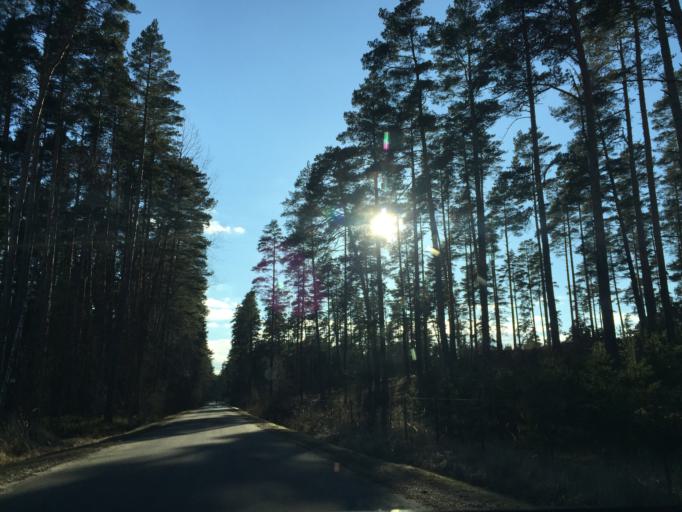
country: LV
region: Babite
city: Pinki
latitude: 56.9248
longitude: 23.8957
